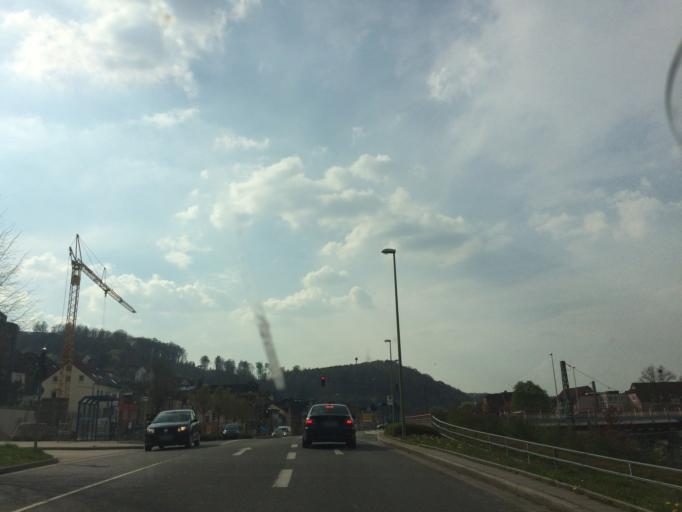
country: DE
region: North Rhine-Westphalia
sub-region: Regierungsbezirk Arnsberg
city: Nachrodt-Wiblingwerde
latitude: 51.3482
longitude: 7.5737
